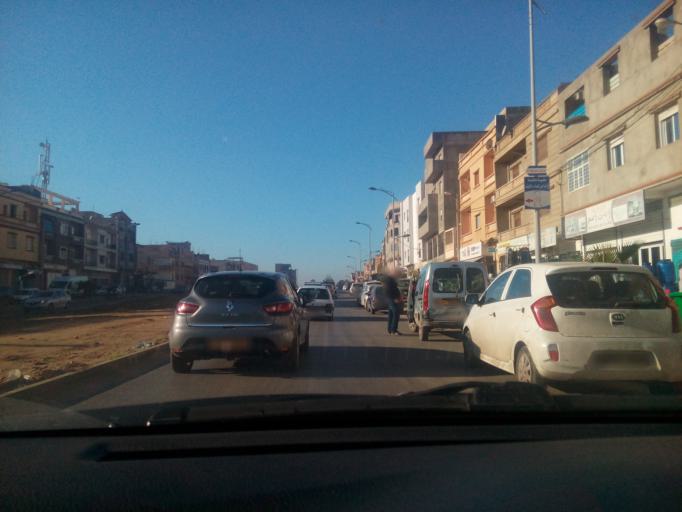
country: DZ
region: Oran
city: Bir el Djir
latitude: 35.7464
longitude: -0.5593
